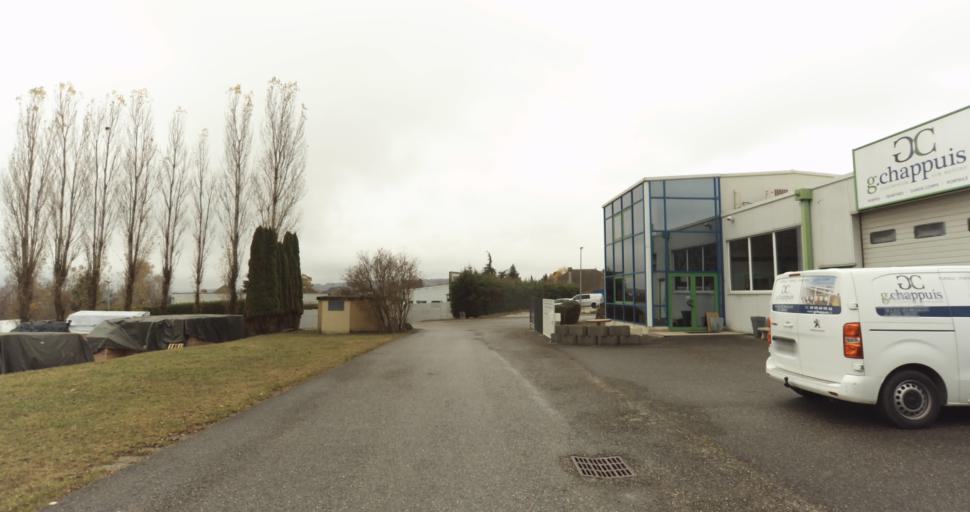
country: FR
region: Rhone-Alpes
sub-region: Departement de la Haute-Savoie
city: Groisy
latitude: 46.0108
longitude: 6.1652
